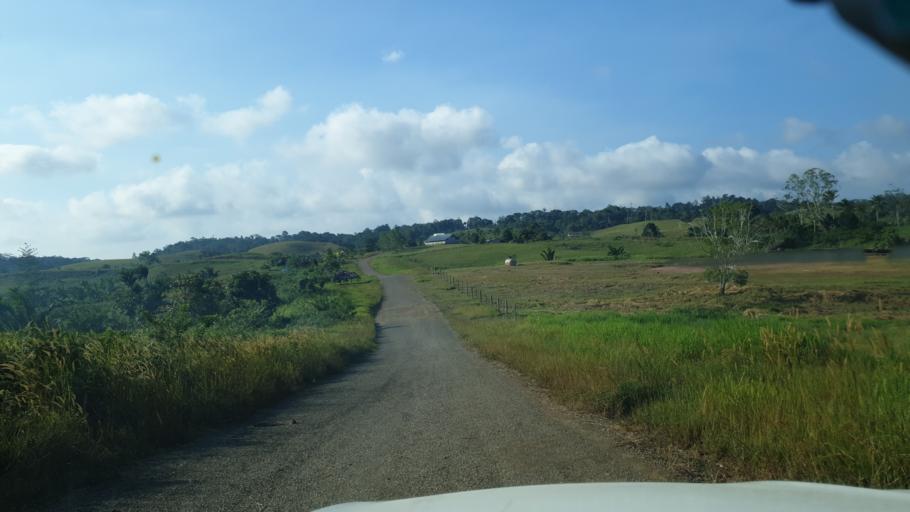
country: PG
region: East Sepik
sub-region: Wewak
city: Wewak
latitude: -3.7059
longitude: 143.7217
